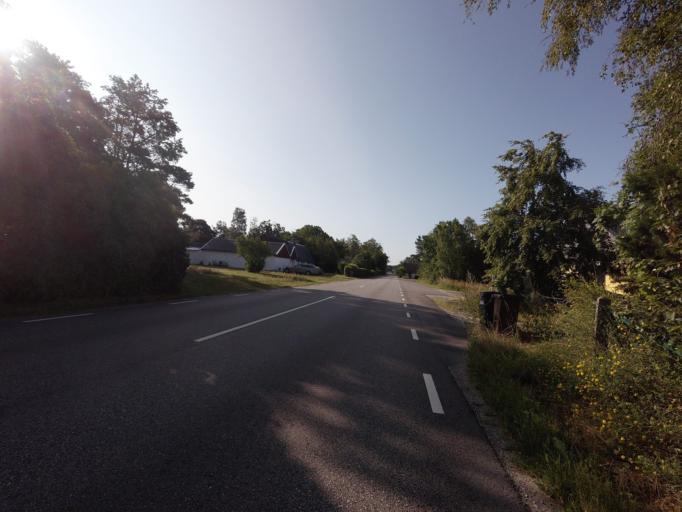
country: SE
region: Skane
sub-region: Kavlinge Kommun
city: Hofterup
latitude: 55.8303
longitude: 12.9641
